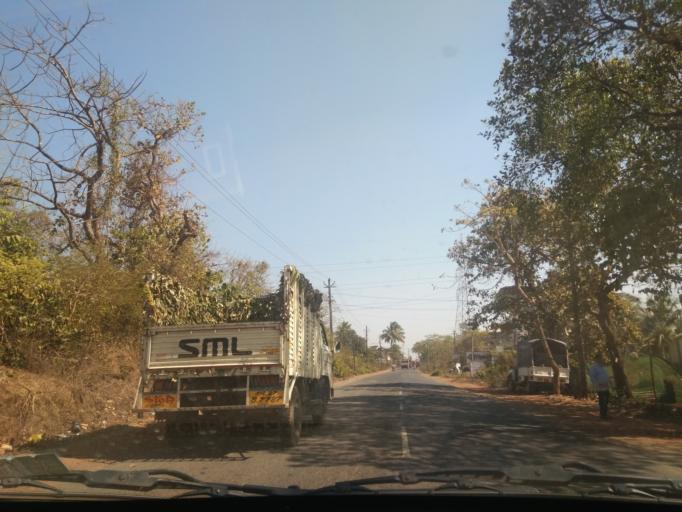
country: IN
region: Goa
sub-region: North Goa
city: Carapur
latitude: 15.5729
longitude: 73.9971
